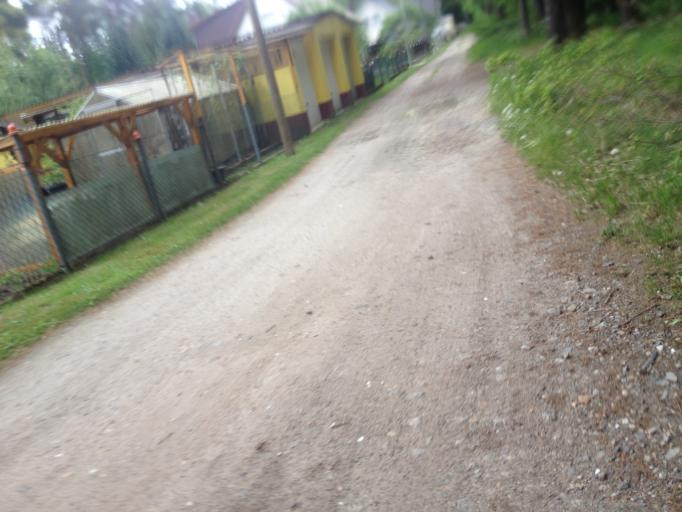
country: DE
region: Brandenburg
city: Drehnow
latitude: 51.8154
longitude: 14.3495
